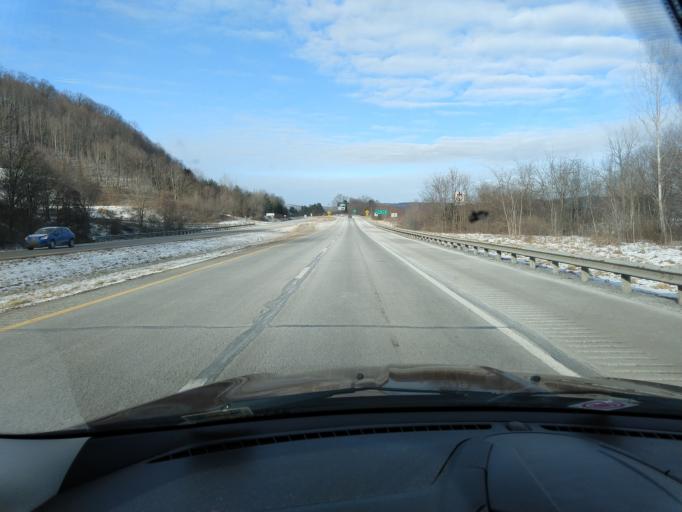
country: US
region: West Virginia
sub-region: Mercer County
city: Princeton
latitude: 37.3628
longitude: -81.0760
